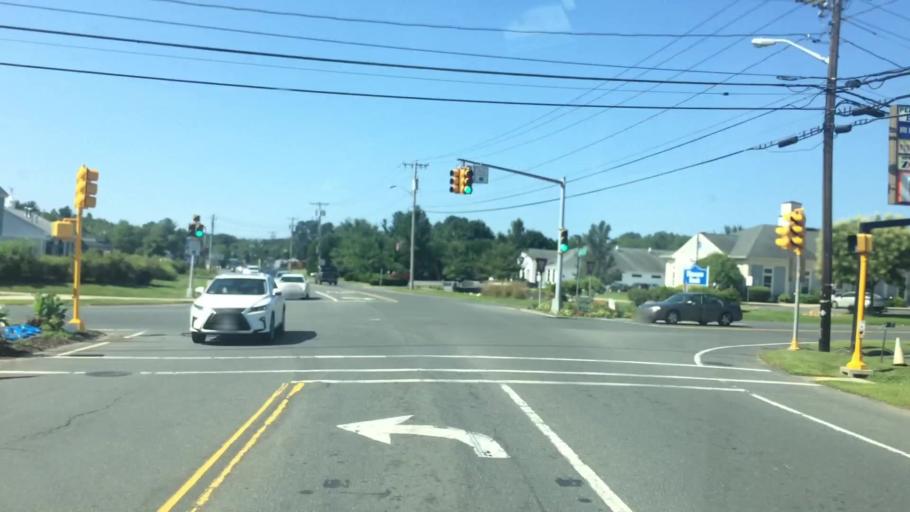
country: US
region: Massachusetts
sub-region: Hampshire County
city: Granby
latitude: 42.2470
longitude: -72.5440
